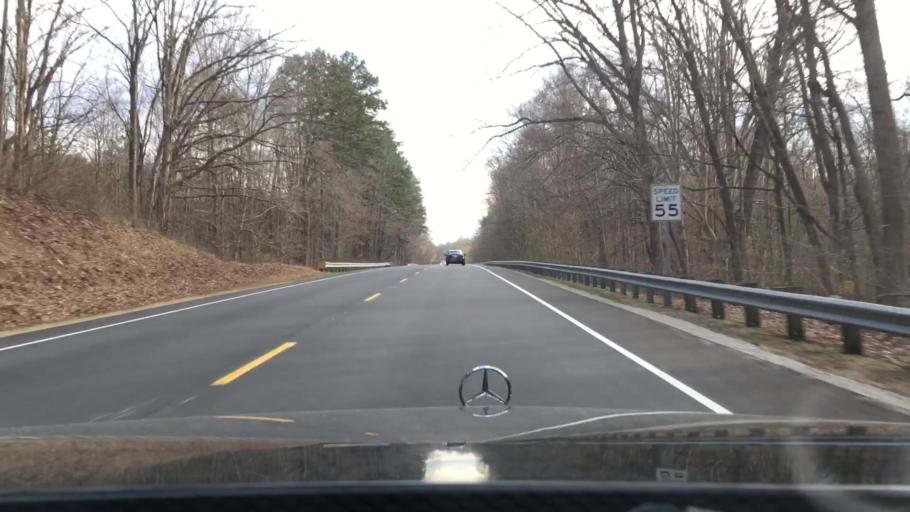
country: US
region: North Carolina
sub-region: Caswell County
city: Yanceyville
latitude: 36.4734
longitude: -79.3774
